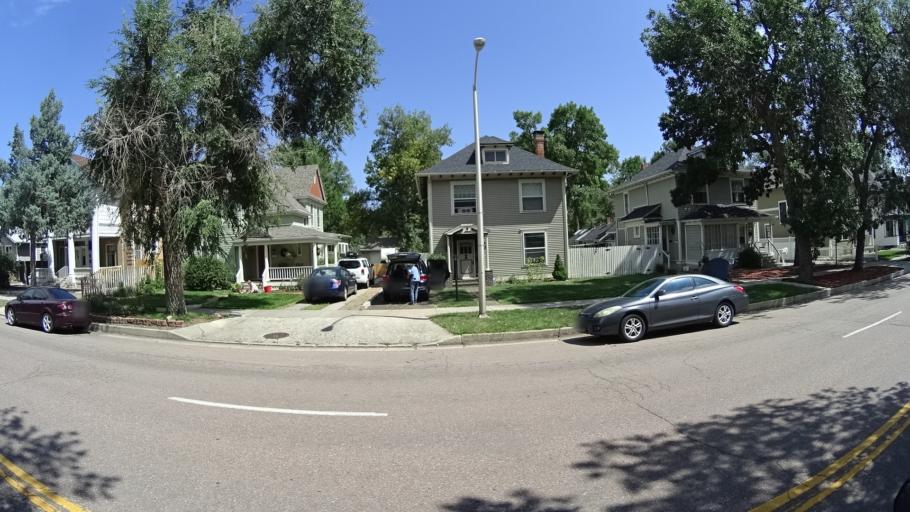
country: US
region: Colorado
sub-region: El Paso County
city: Colorado Springs
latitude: 38.8572
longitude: -104.8187
